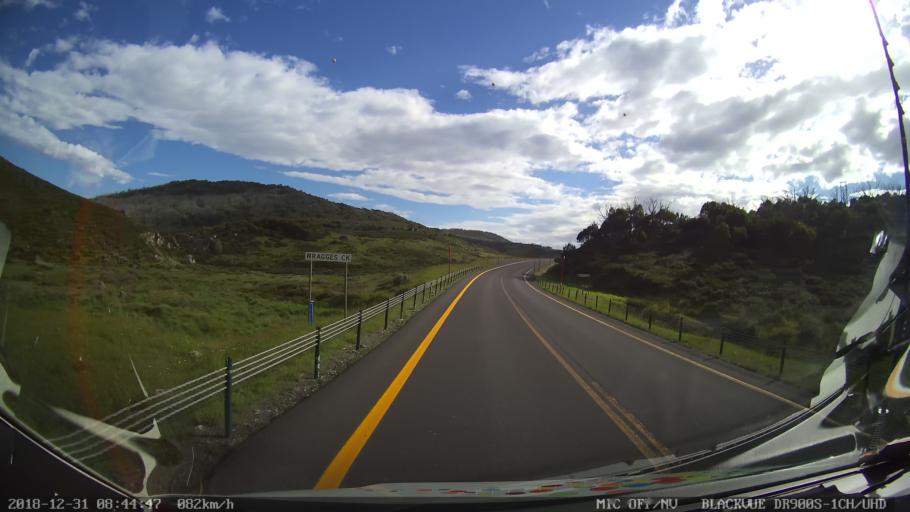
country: AU
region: New South Wales
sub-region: Snowy River
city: Jindabyne
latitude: -36.3806
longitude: 148.4580
